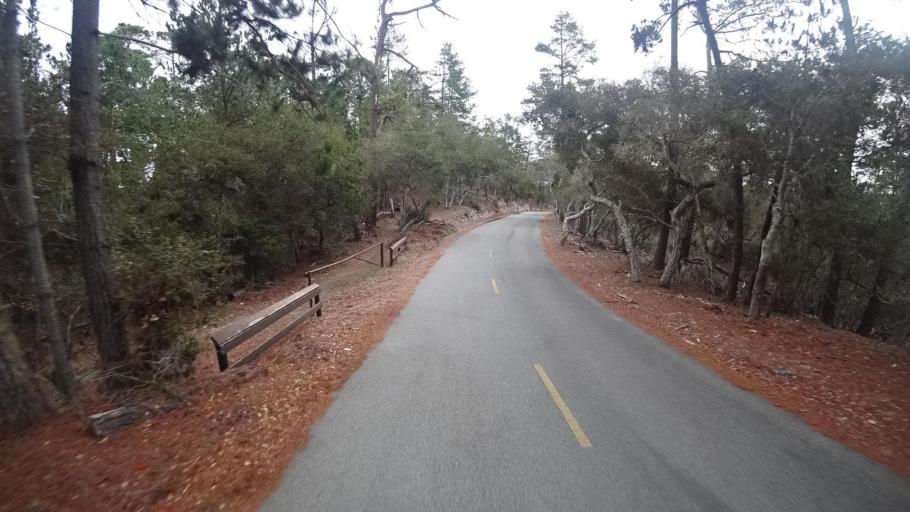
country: US
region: California
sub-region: Monterey County
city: Del Rey Oaks
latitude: 36.5643
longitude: -121.8664
